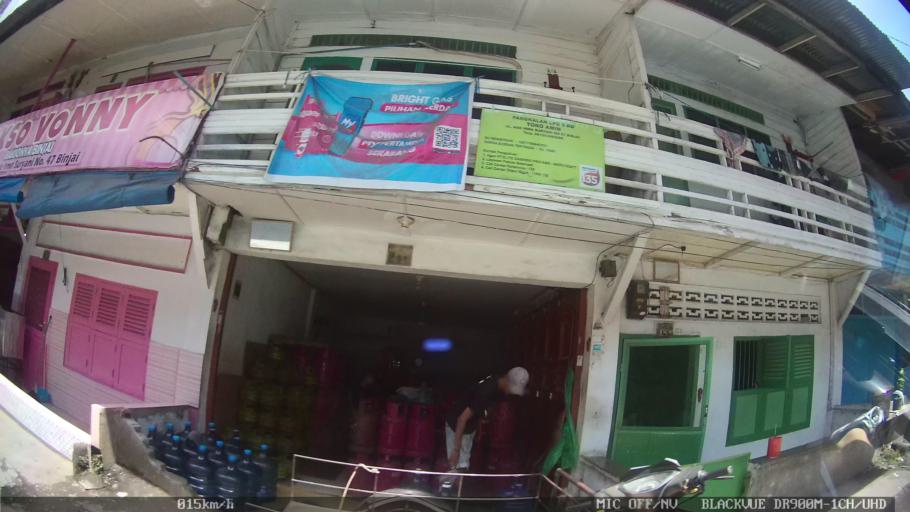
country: ID
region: North Sumatra
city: Binjai
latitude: 3.6116
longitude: 98.4911
